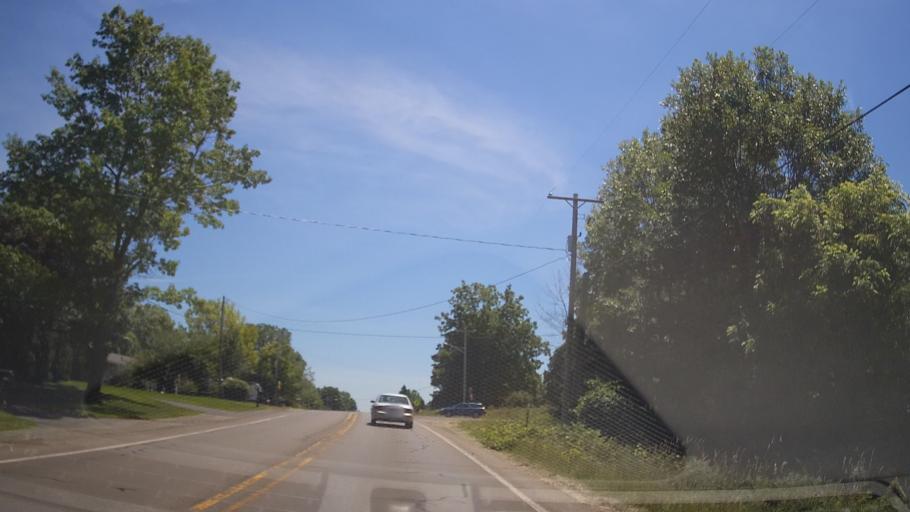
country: US
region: Michigan
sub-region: Grand Traverse County
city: Traverse City
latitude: 44.7058
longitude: -85.6925
